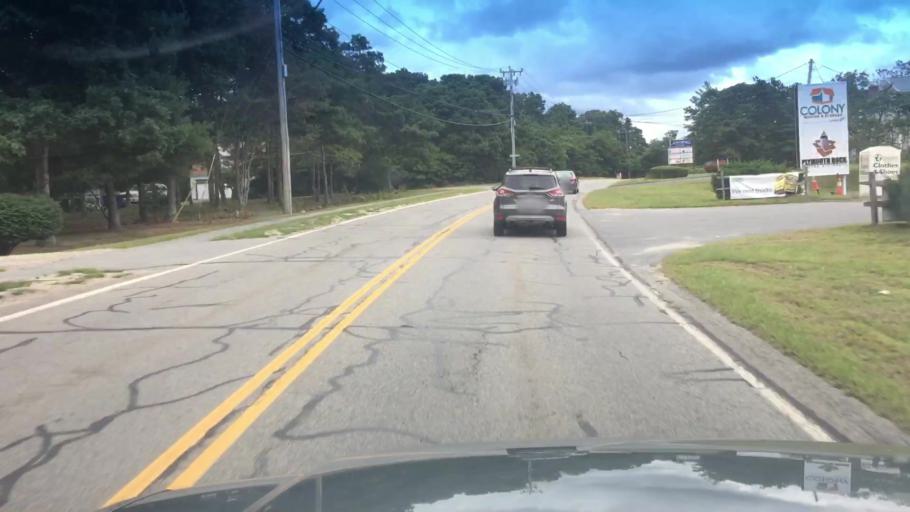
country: US
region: Massachusetts
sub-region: Barnstable County
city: Pocasset
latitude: 41.6965
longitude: -70.5919
